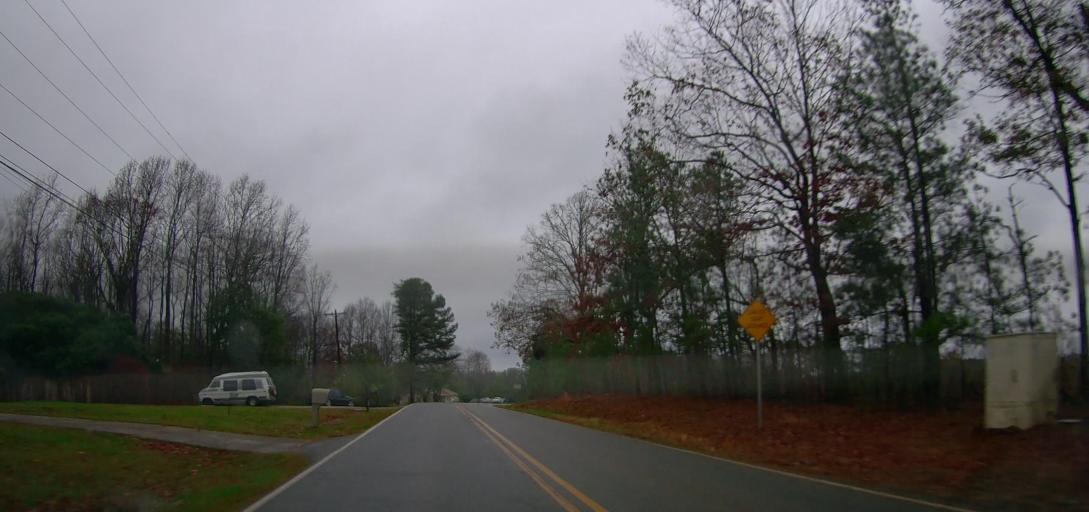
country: US
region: Georgia
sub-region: Banks County
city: Alto
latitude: 34.5103
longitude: -83.5903
